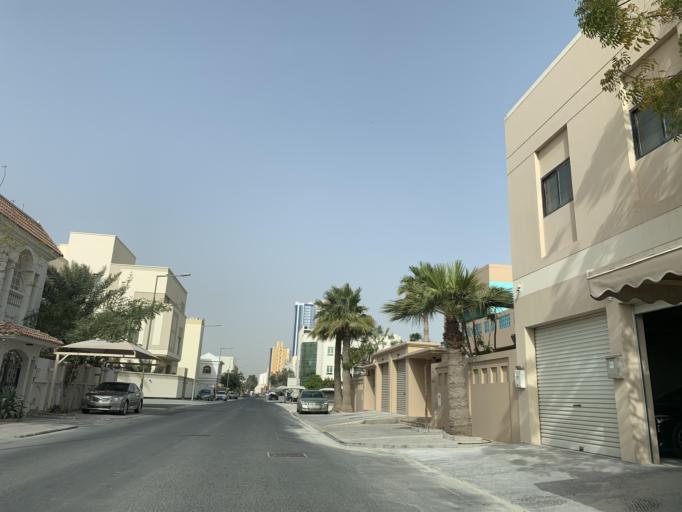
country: BH
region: Manama
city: Manama
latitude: 26.2110
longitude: 50.6165
